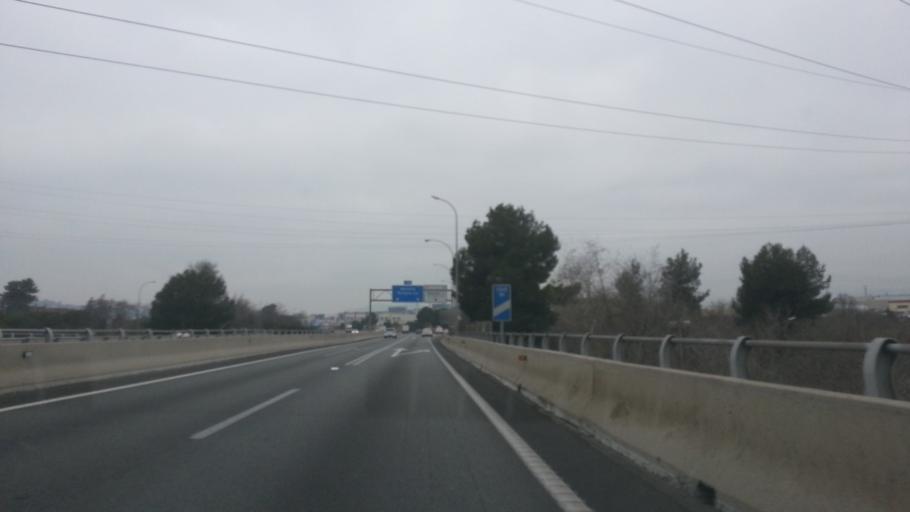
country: ES
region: Catalonia
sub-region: Provincia de Barcelona
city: Terrassa
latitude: 41.5449
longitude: 2.0393
